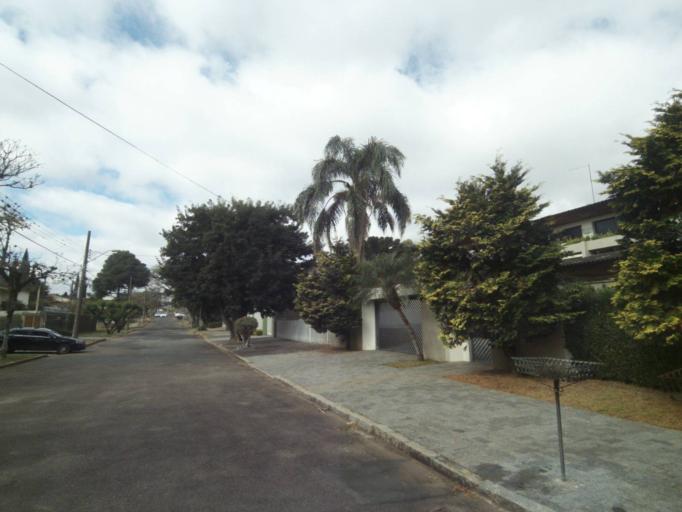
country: BR
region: Parana
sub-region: Curitiba
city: Curitiba
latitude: -25.4468
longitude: -49.3125
